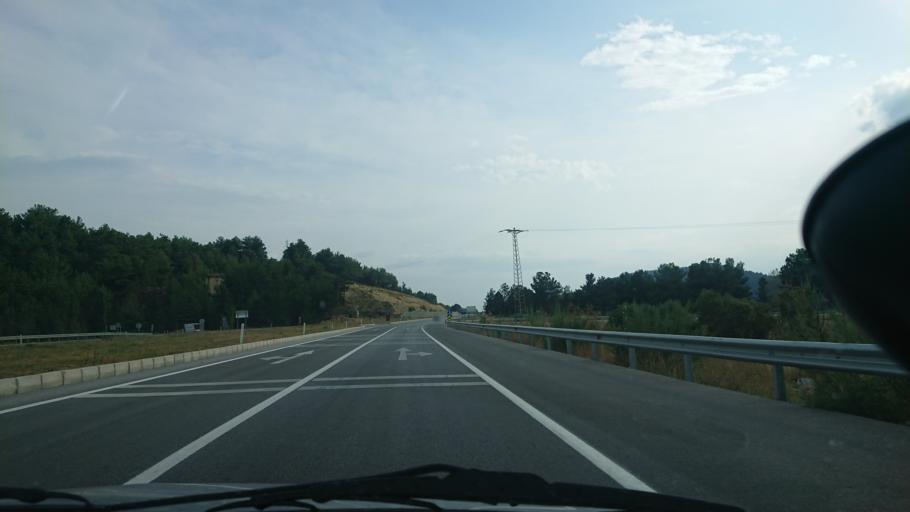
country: TR
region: Kuetahya
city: Gediz
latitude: 38.9266
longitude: 29.3048
